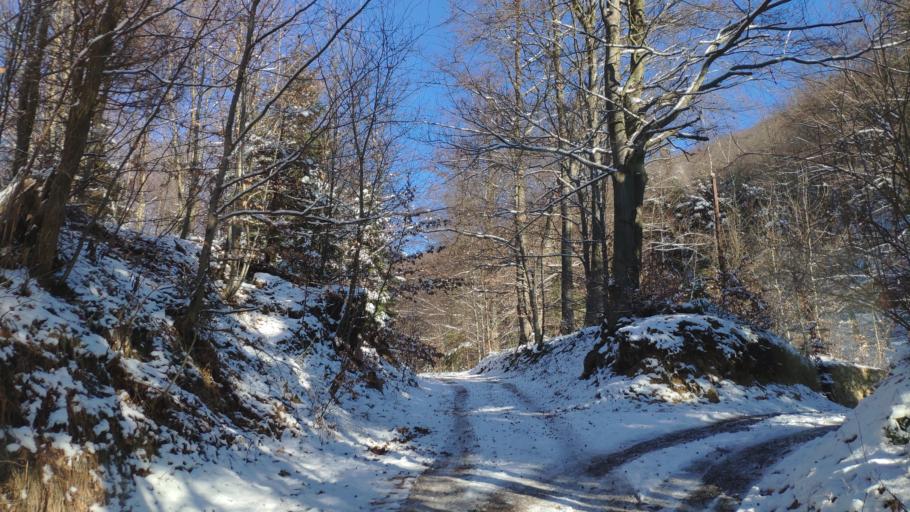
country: SK
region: Kosicky
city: Gelnica
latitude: 48.7575
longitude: 21.0065
